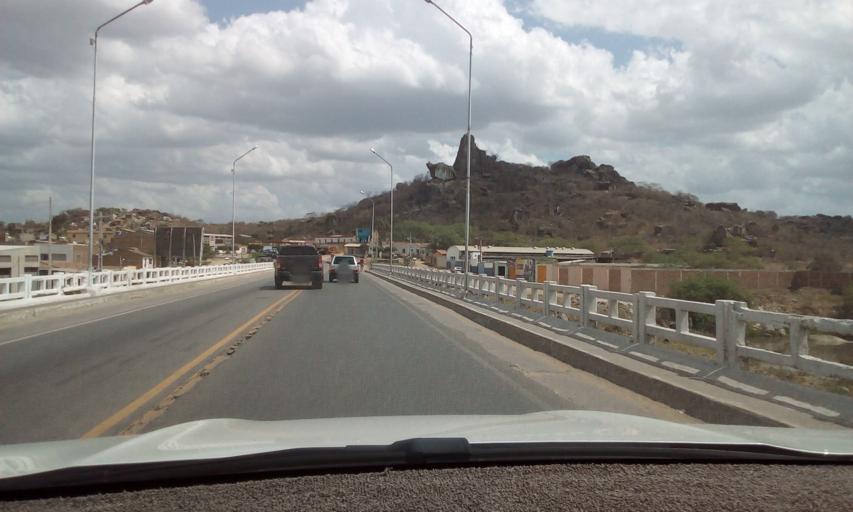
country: BR
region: Pernambuco
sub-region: Toritama
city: Toritama
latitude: -8.0116
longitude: -36.0574
